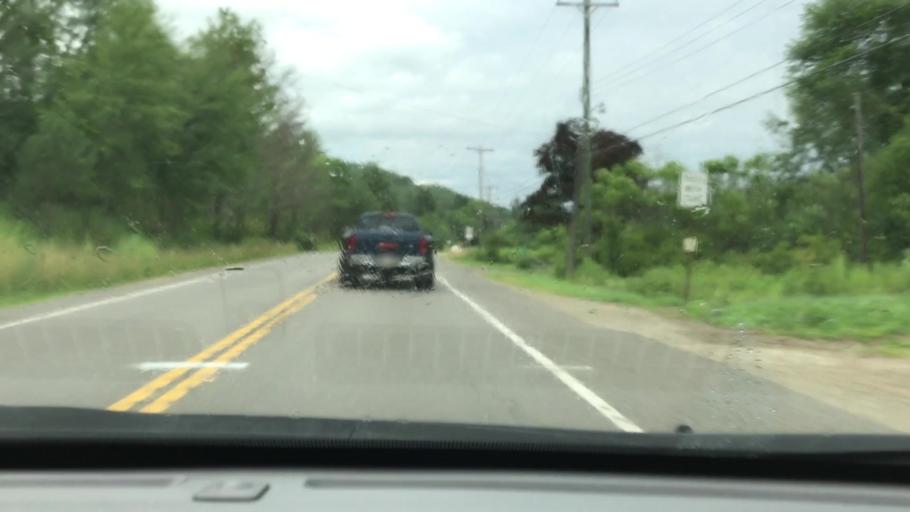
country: US
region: Pennsylvania
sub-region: McKean County
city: Bradford
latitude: 41.9004
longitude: -78.6525
